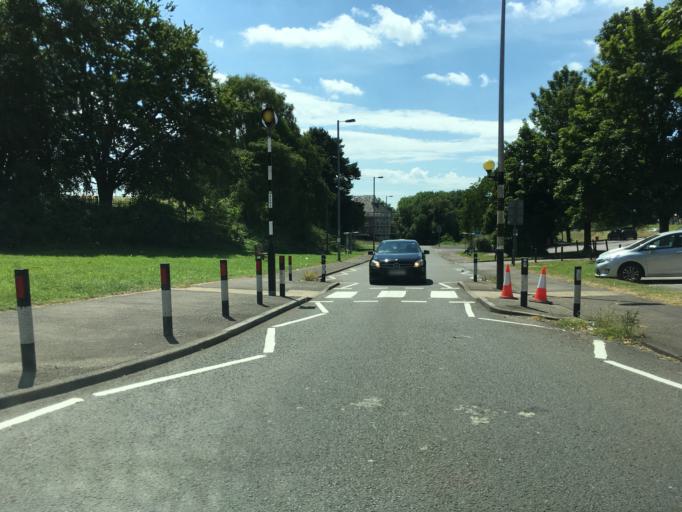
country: GB
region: Wales
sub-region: Newport
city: Newport
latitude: 51.5775
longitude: -3.0188
